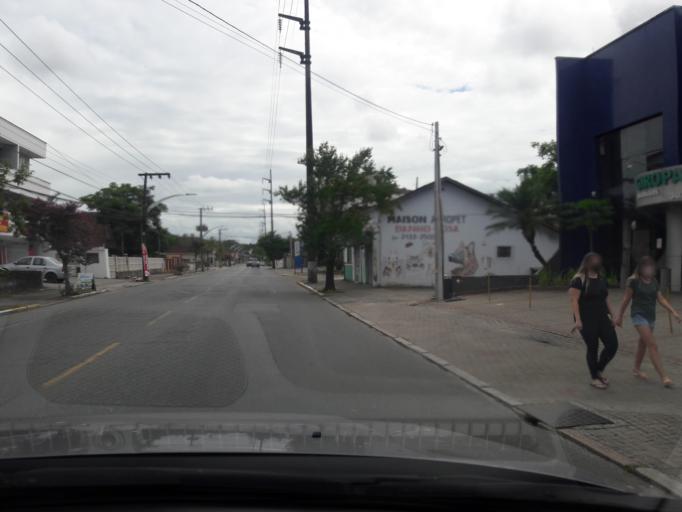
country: BR
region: Santa Catarina
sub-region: Joinville
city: Joinville
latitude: -26.3187
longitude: -48.8501
